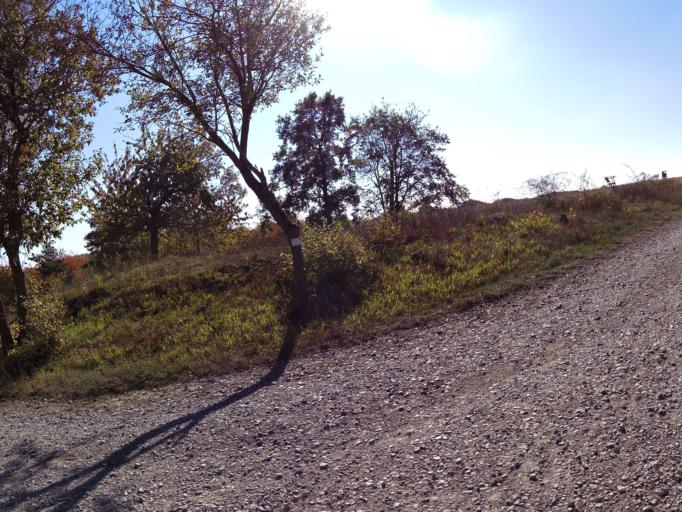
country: DE
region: Bavaria
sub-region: Regierungsbezirk Unterfranken
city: Eibelstadt
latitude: 49.7156
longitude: 9.9902
